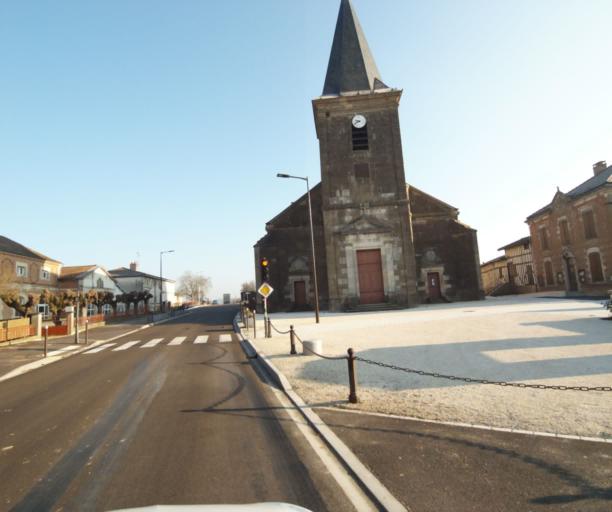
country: FR
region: Champagne-Ardenne
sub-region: Departement de la Haute-Marne
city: Montier-en-Der
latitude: 48.4341
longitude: 4.7248
